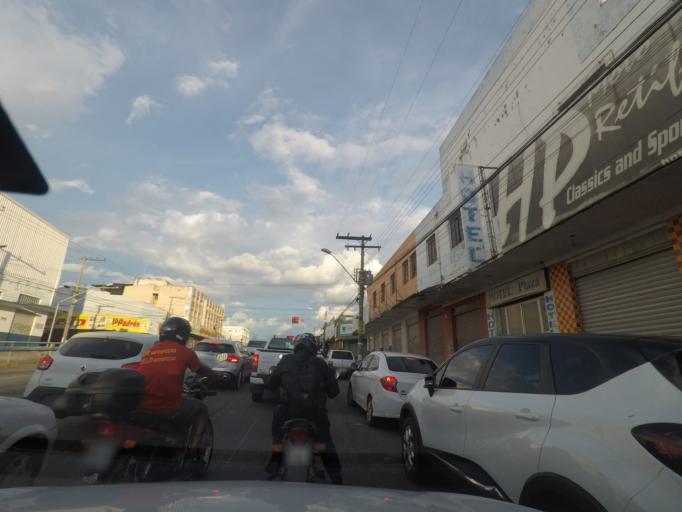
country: BR
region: Goias
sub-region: Goiania
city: Goiania
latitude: -16.6708
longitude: -49.2961
